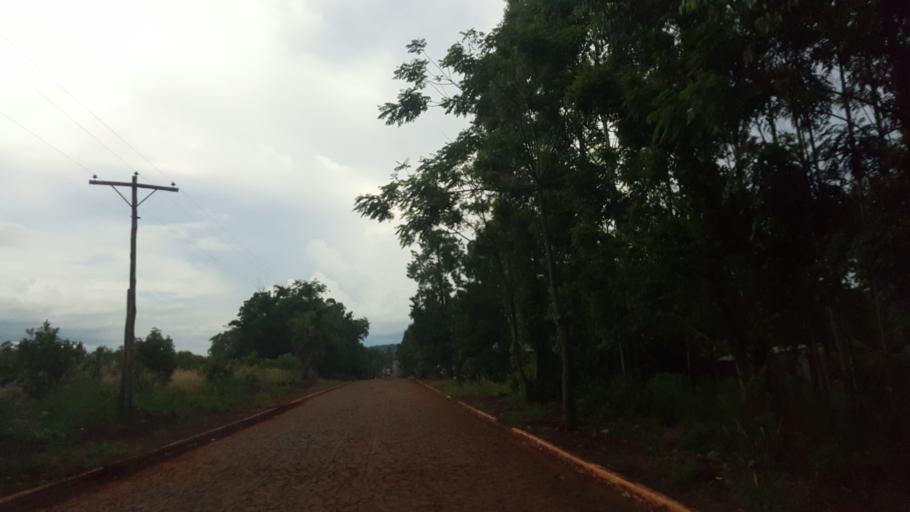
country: AR
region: Misiones
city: Jardin America
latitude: -27.0760
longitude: -55.2864
